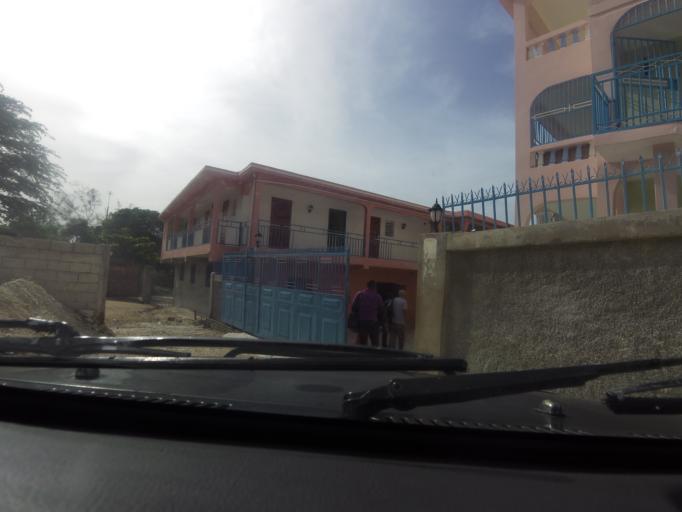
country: HT
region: Ouest
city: Anse a Galets
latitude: 18.8329
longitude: -72.8635
